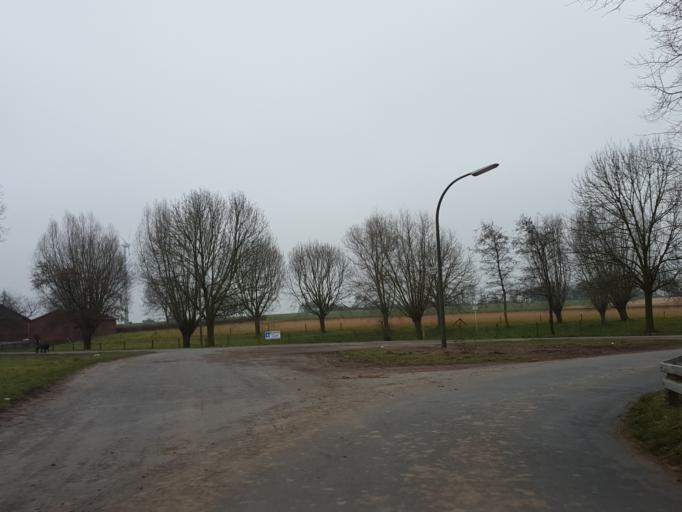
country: DE
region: North Rhine-Westphalia
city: Oer-Erkenschwick
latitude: 51.6272
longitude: 7.2613
